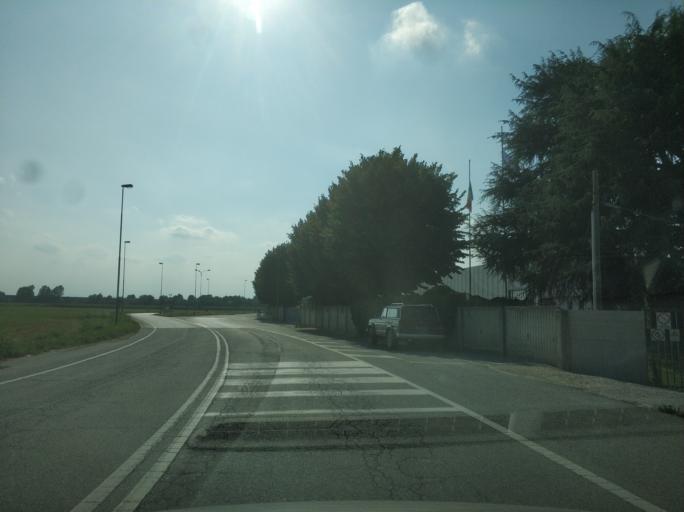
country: IT
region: Piedmont
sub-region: Provincia di Cuneo
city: Bra
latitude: 44.6993
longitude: 7.8321
